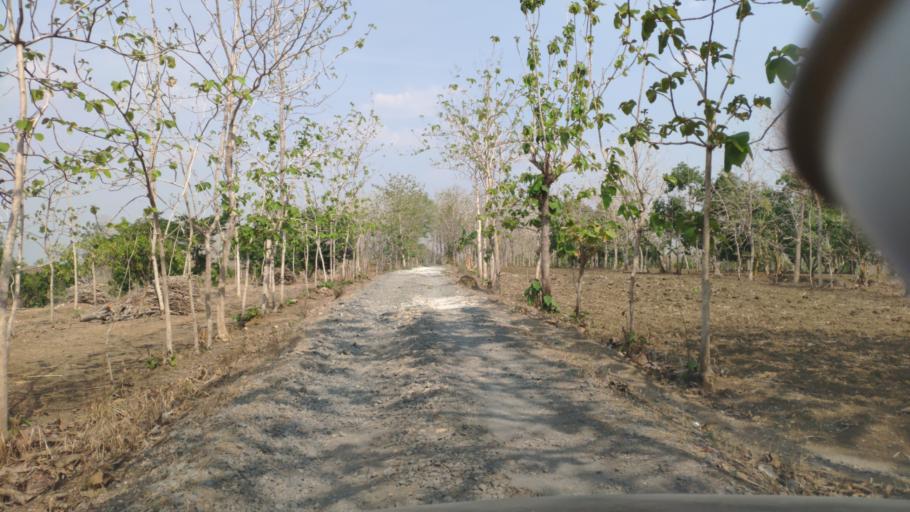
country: ID
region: Central Java
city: Jagong
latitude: -7.0982
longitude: 111.2263
